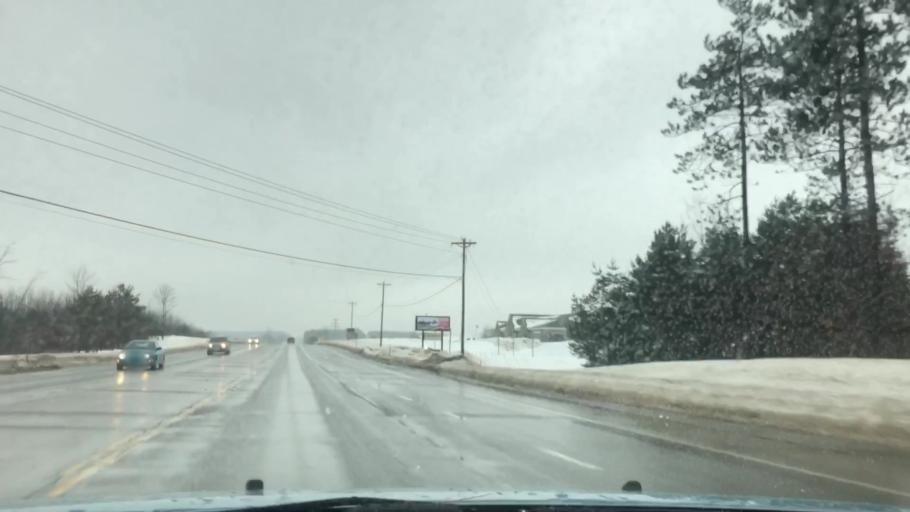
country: US
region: Michigan
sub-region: Otsego County
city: Gaylord
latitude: 45.0276
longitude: -84.7135
